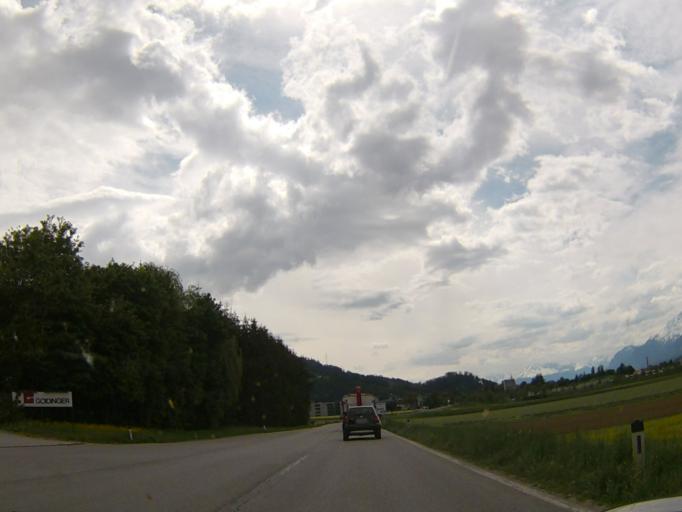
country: AT
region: Tyrol
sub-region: Politischer Bezirk Innsbruck Land
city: Wattenberg
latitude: 47.2951
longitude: 11.6106
